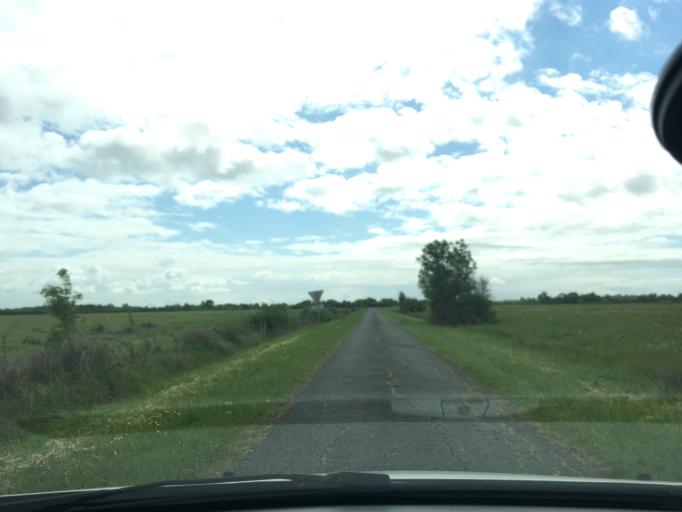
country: FR
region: Aquitaine
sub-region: Departement de la Gironde
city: Saint-Estephe
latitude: 45.3323
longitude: -0.8087
